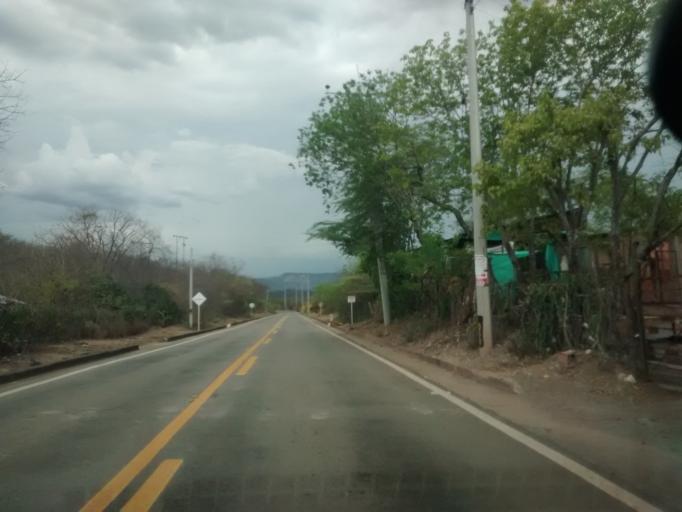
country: CO
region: Cundinamarca
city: Agua de Dios
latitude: 4.4280
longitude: -74.6949
